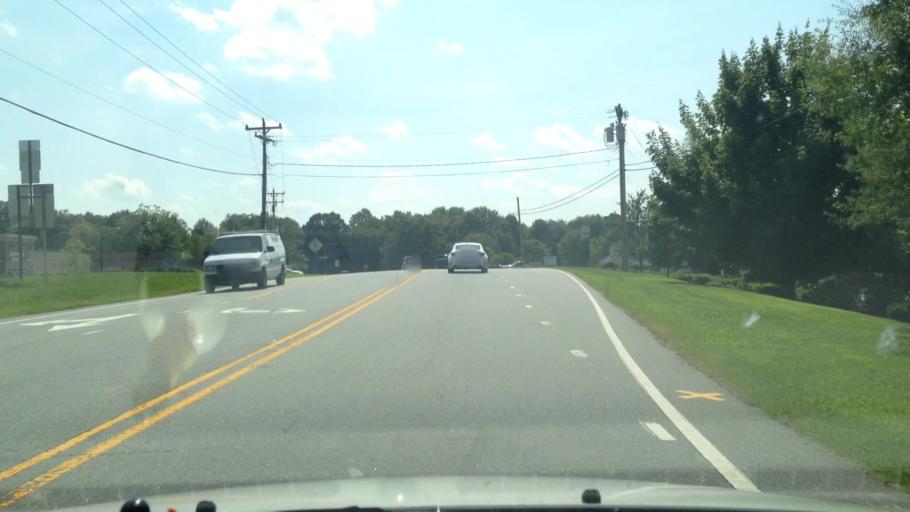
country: US
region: North Carolina
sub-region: Guilford County
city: Oak Ridge
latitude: 36.1734
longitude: -79.9897
